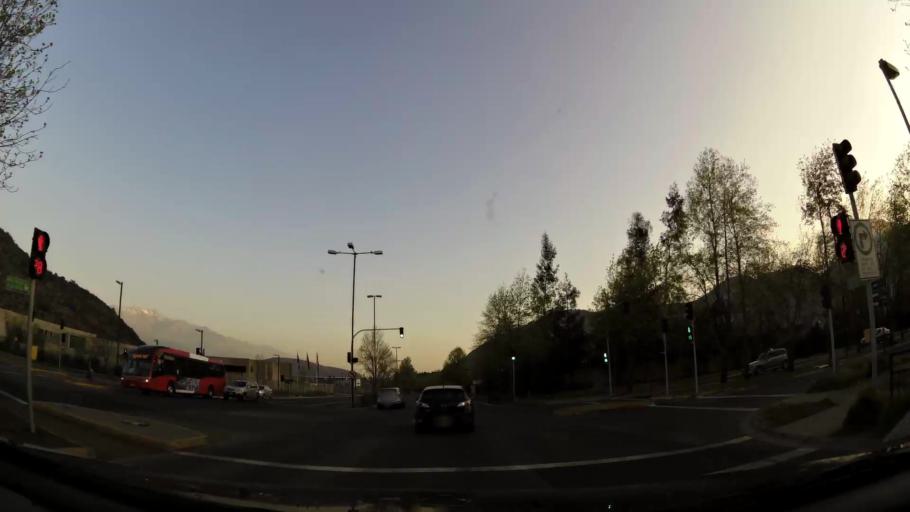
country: CL
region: Santiago Metropolitan
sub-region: Provincia de Chacabuco
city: Chicureo Abajo
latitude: -33.3370
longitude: -70.5459
